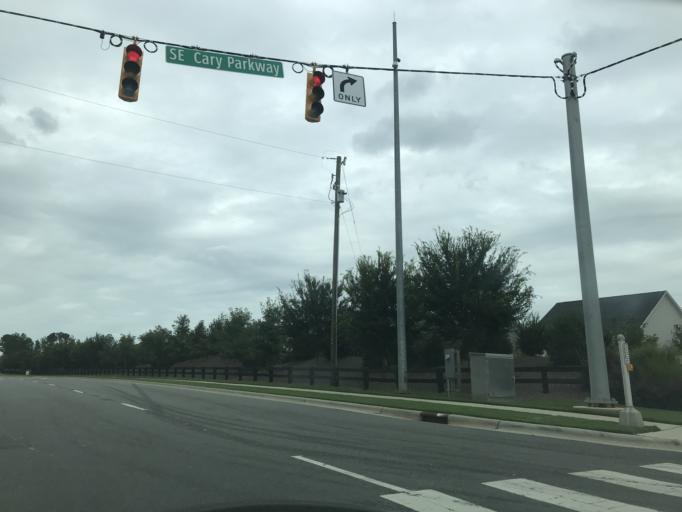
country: US
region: North Carolina
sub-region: Wake County
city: Cary
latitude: 35.7373
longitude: -78.7440
